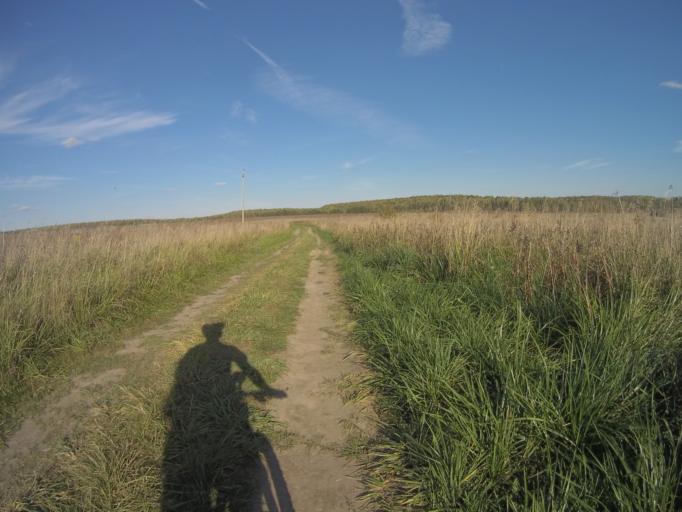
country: RU
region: Vladimir
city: Golovino
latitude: 55.9778
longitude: 40.4537
